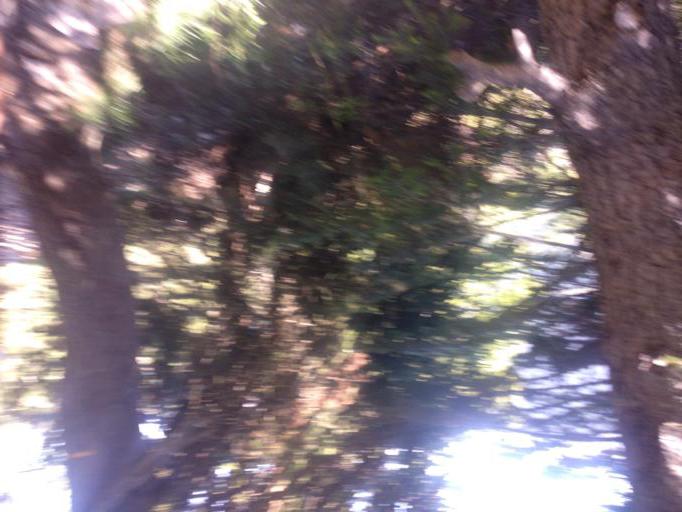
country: FR
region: Rhone-Alpes
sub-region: Departement de l'Isere
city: Le Sappey-en-Chartreuse
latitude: 45.2859
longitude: 5.7827
